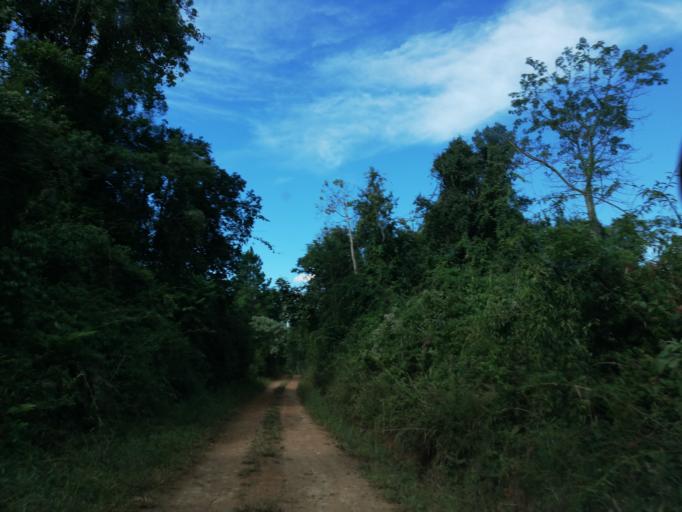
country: AR
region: Misiones
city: Dos de Mayo
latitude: -27.0155
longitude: -54.4268
